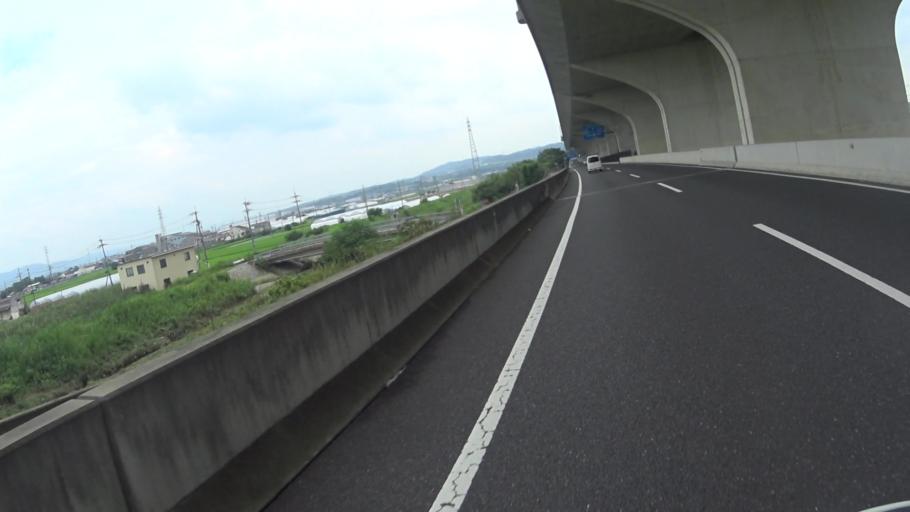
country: JP
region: Kyoto
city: Yawata
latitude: 34.8617
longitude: 135.7350
